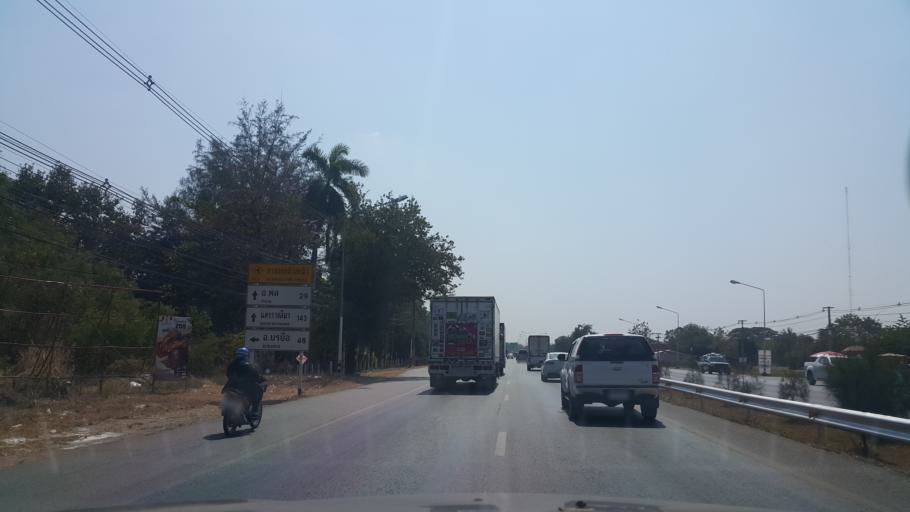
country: TH
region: Khon Kaen
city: Ban Phai
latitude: 16.0490
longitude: 102.7152
